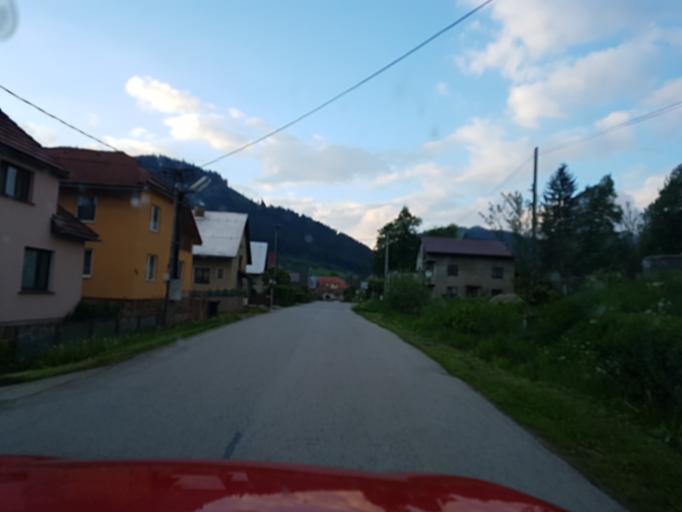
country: SK
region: Zilinsky
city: Ruzomberok
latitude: 49.1224
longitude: 19.4132
